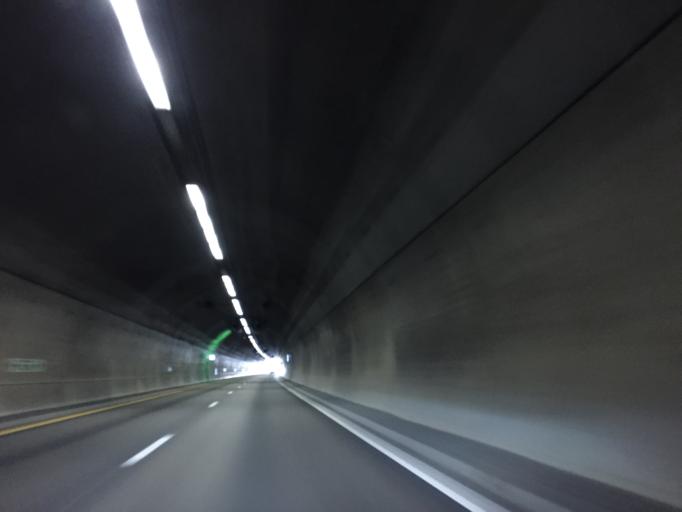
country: NO
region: Akershus
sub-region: Vestby
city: Vestby
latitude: 59.5348
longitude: 10.7281
